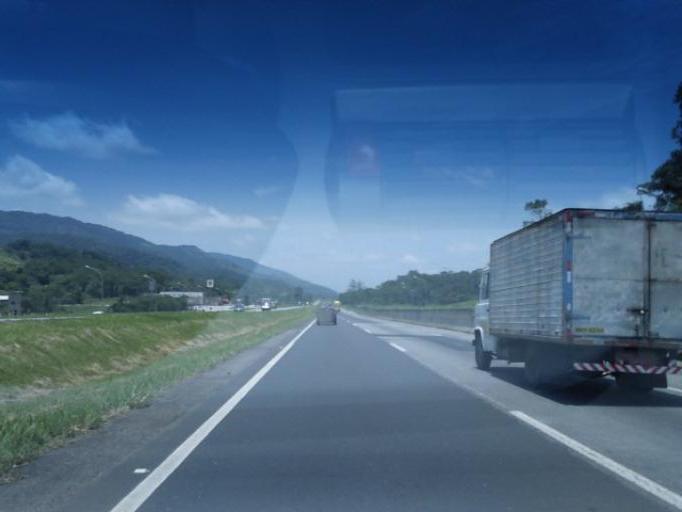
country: BR
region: Sao Paulo
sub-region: Miracatu
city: Miracatu
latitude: -24.2716
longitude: -47.4039
